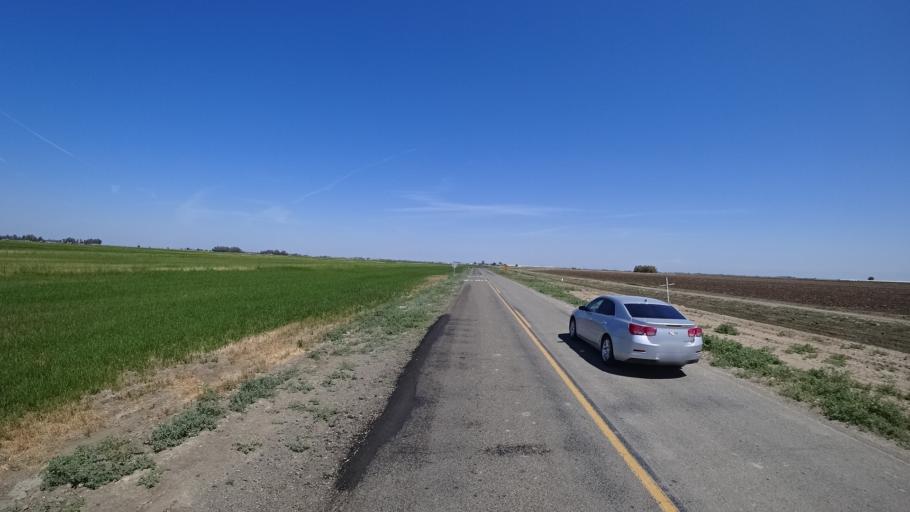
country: US
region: California
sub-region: Kings County
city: Stratford
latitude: 36.1905
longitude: -119.7627
